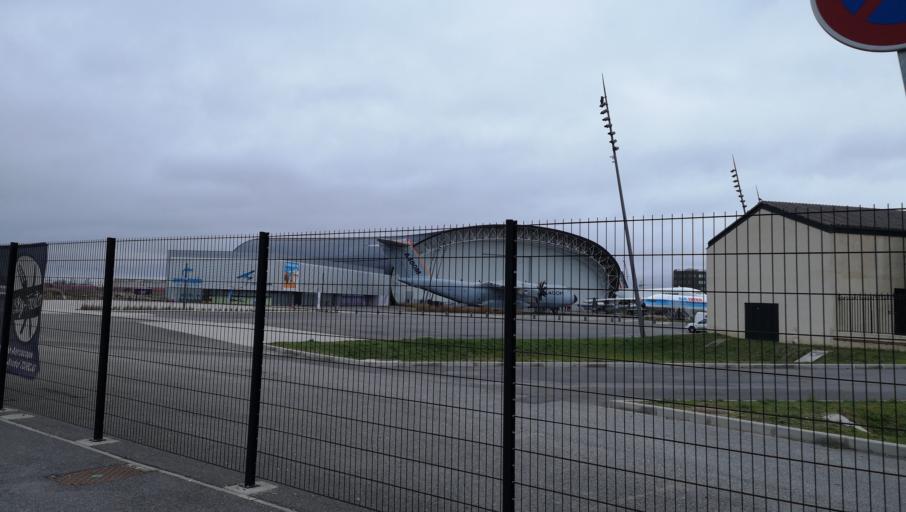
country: FR
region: Midi-Pyrenees
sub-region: Departement de la Haute-Garonne
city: Beauzelle
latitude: 43.6587
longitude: 1.3585
